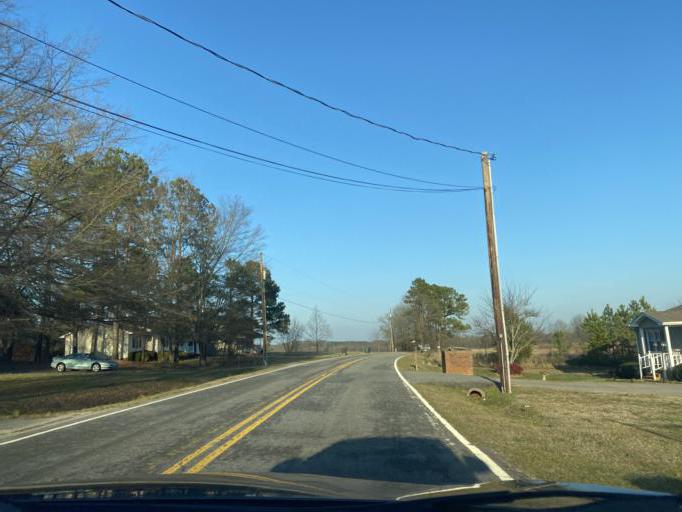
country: US
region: South Carolina
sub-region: Cherokee County
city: Gaffney
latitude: 35.1087
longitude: -81.6682
